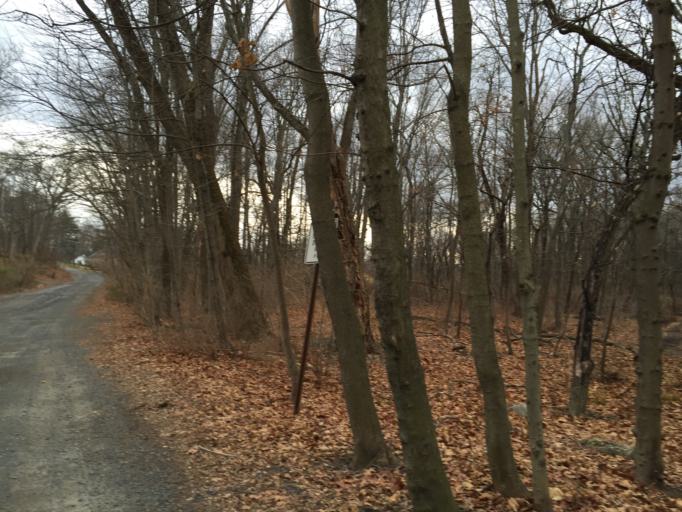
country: US
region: New Jersey
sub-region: Morris County
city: Chatham
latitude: 40.7258
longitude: -74.3898
